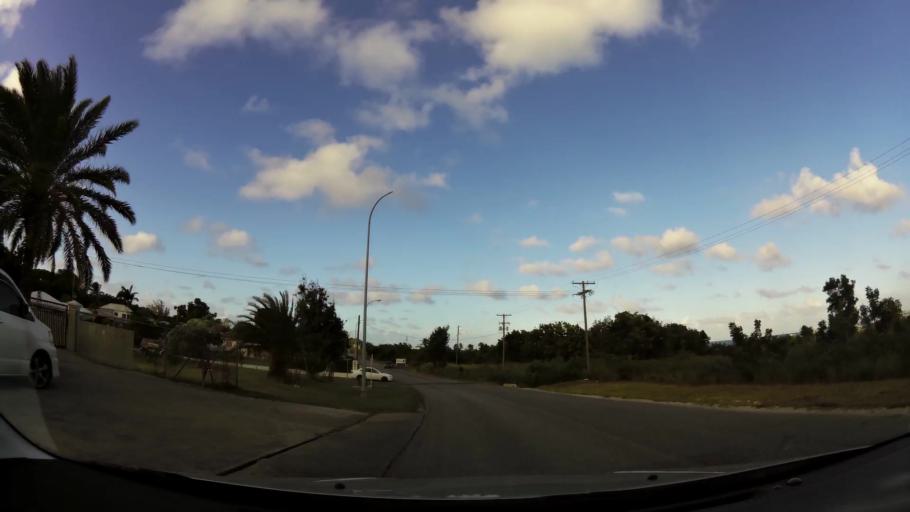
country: AG
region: Saint George
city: Piggotts
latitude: 17.1454
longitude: -61.7949
